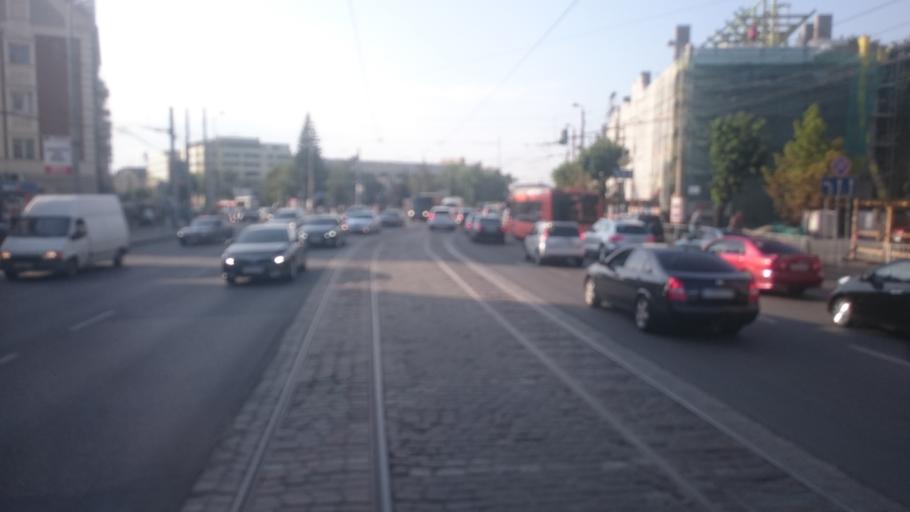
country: RU
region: Kaliningrad
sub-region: Gorod Kaliningrad
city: Kaliningrad
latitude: 54.7157
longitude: 20.5035
